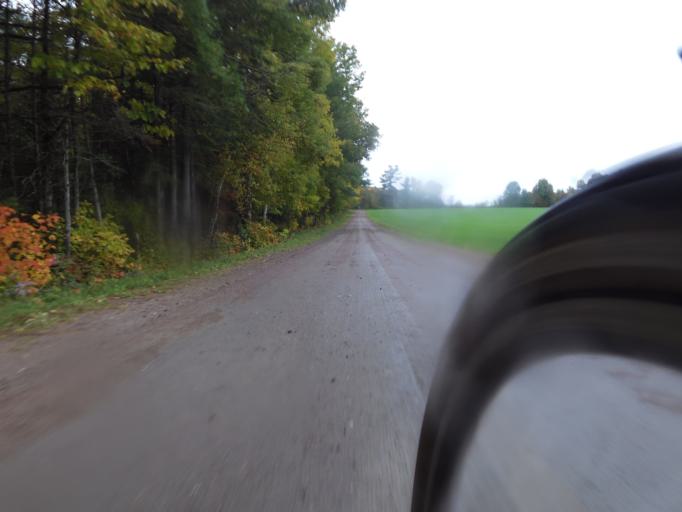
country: CA
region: Quebec
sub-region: Outaouais
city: Shawville
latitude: 45.6791
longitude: -76.5455
